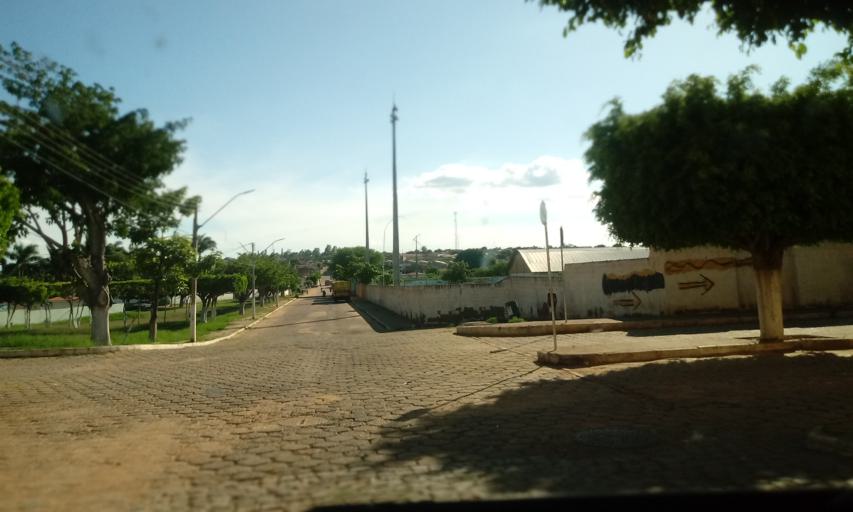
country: BR
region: Bahia
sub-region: Riacho De Santana
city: Riacho de Santana
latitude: -13.7737
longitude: -42.7172
